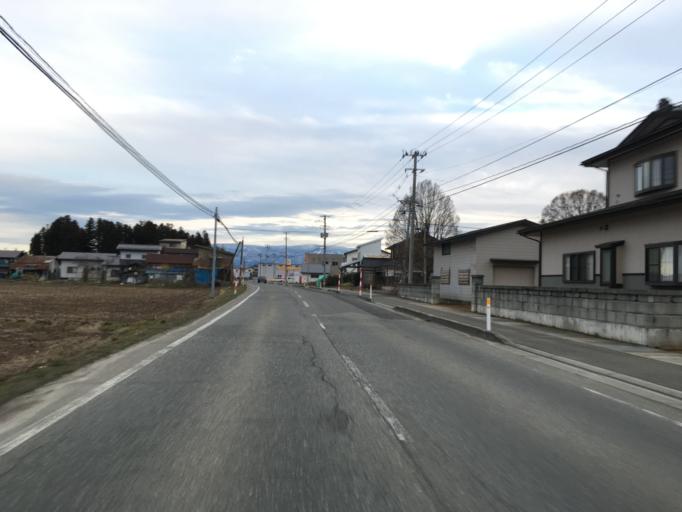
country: JP
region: Yamagata
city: Yonezawa
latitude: 37.9857
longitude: 140.0771
